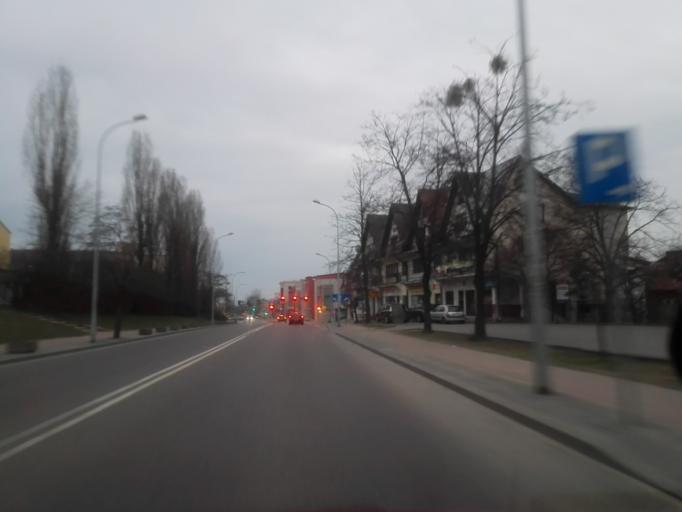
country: PL
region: Podlasie
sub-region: Lomza
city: Lomza
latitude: 53.1792
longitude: 22.0747
